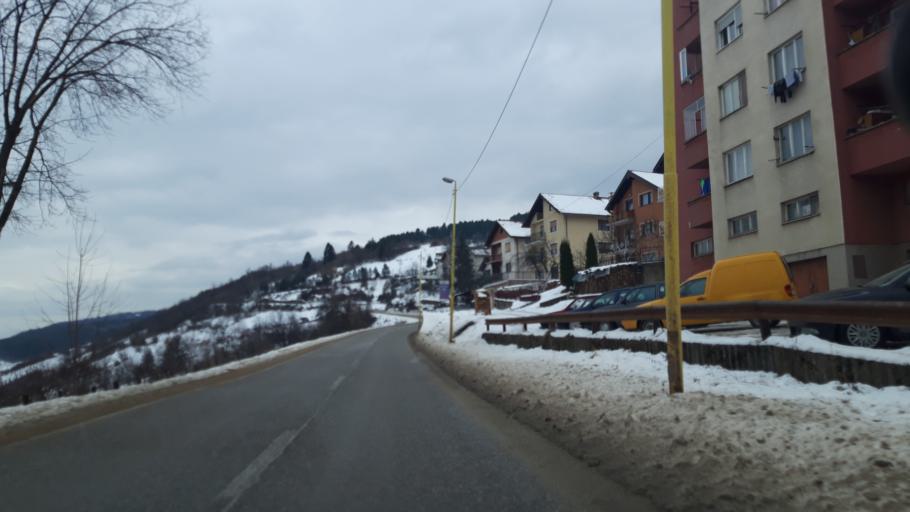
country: BA
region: Republika Srpska
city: Vlasenica
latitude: 44.1821
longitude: 18.9450
